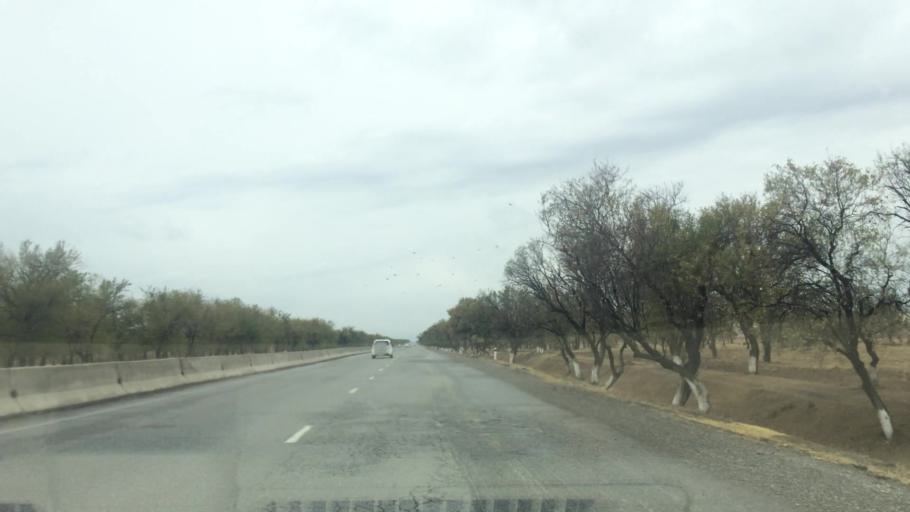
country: UZ
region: Samarqand
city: Bulung'ur
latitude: 39.8308
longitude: 67.4125
